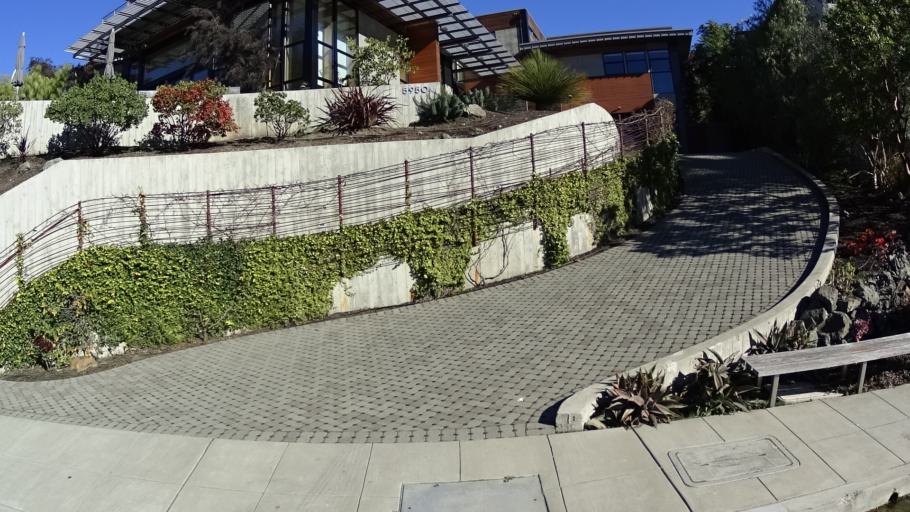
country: US
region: California
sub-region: Alameda County
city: Piedmont
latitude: 37.8449
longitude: -122.2408
